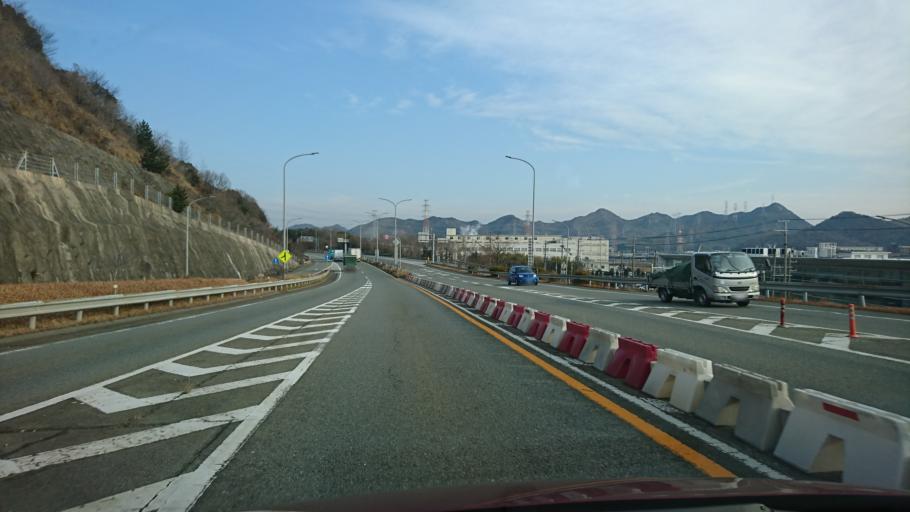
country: JP
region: Hyogo
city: Shirahamacho-usazakiminami
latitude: 34.8019
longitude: 134.7433
